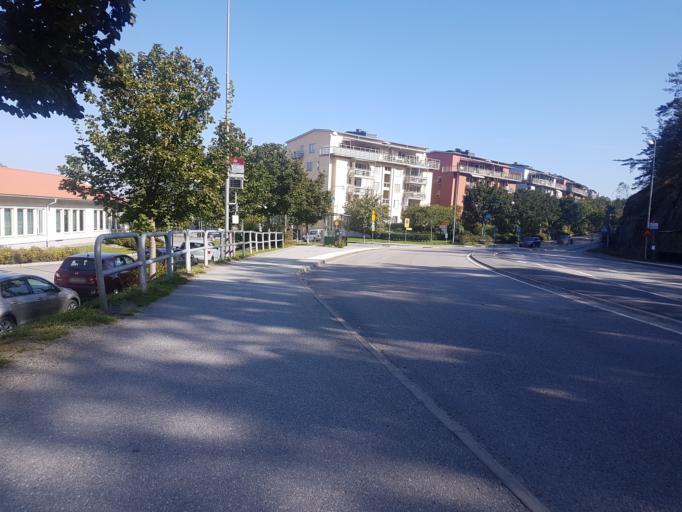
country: SE
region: Stockholm
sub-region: Stockholms Kommun
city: OEstermalm
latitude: 59.3132
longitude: 18.1201
